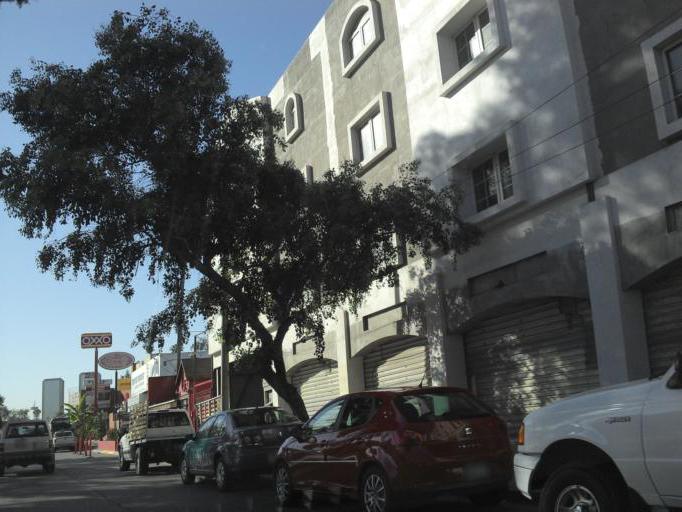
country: MX
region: Baja California
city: Tijuana
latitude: 32.5205
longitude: -117.0150
